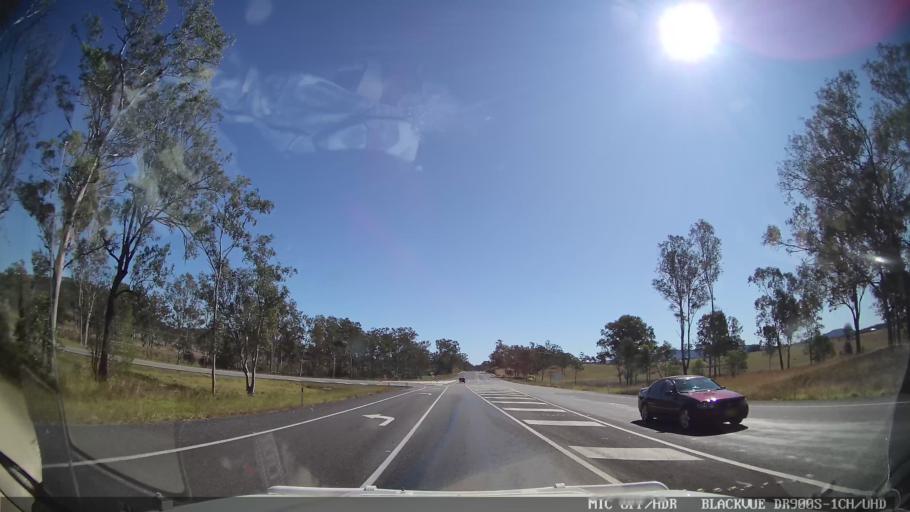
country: AU
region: Queensland
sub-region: Gympie Regional Council
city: Gympie
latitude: -26.0356
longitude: 152.5683
